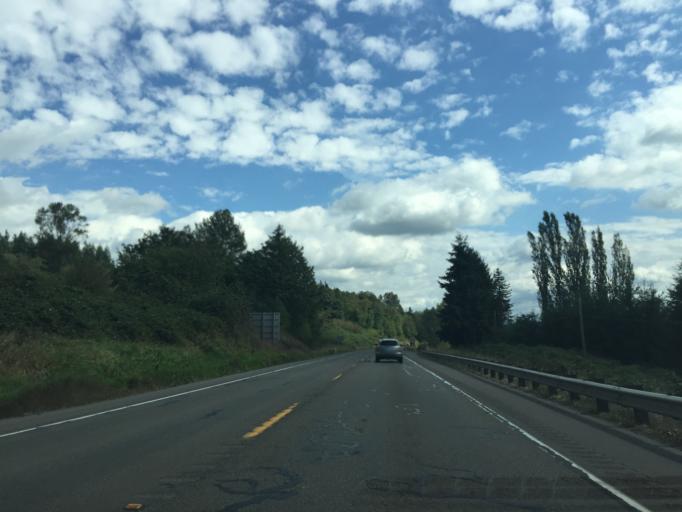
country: US
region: Washington
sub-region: Snohomish County
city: Snohomish
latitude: 47.9110
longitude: -122.0555
